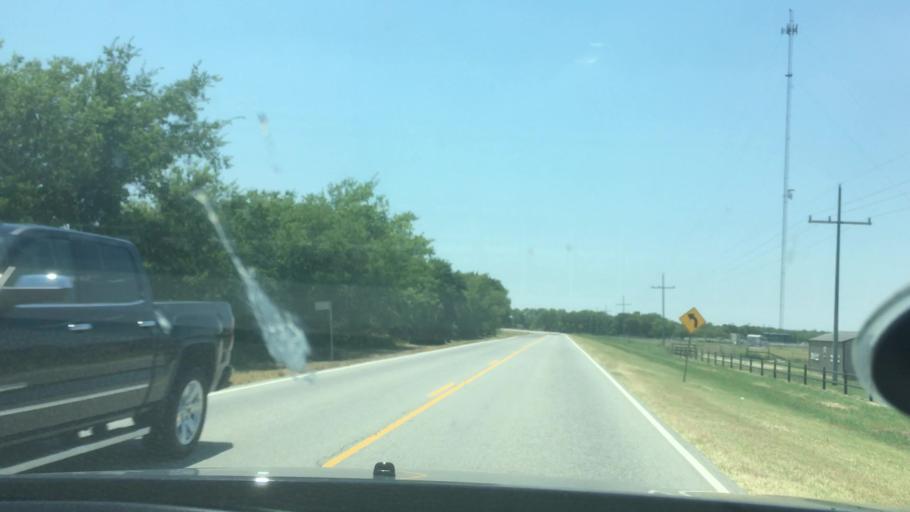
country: US
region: Oklahoma
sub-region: Coal County
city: Coalgate
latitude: 34.4904
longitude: -96.4205
